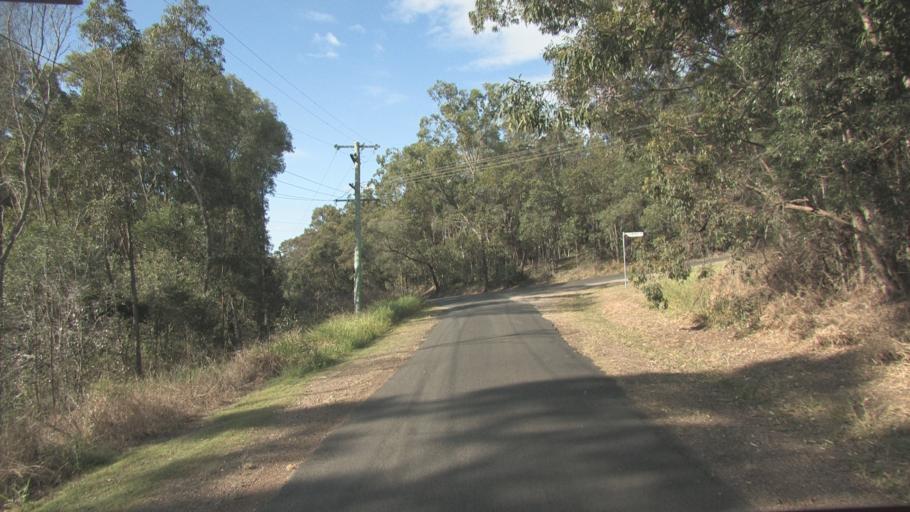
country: AU
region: Queensland
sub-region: Logan
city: Windaroo
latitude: -27.7405
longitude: 153.1648
